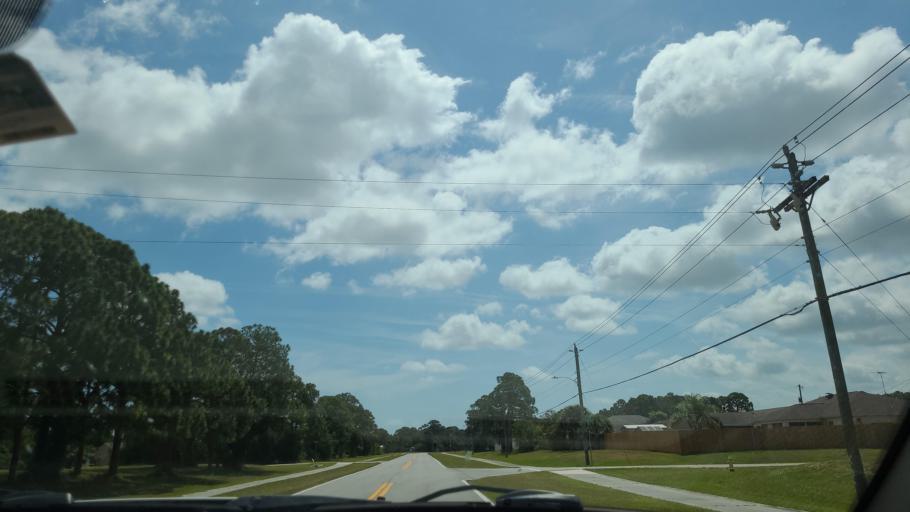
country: US
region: Florida
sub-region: Brevard County
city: West Melbourne
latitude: 28.0314
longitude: -80.6663
